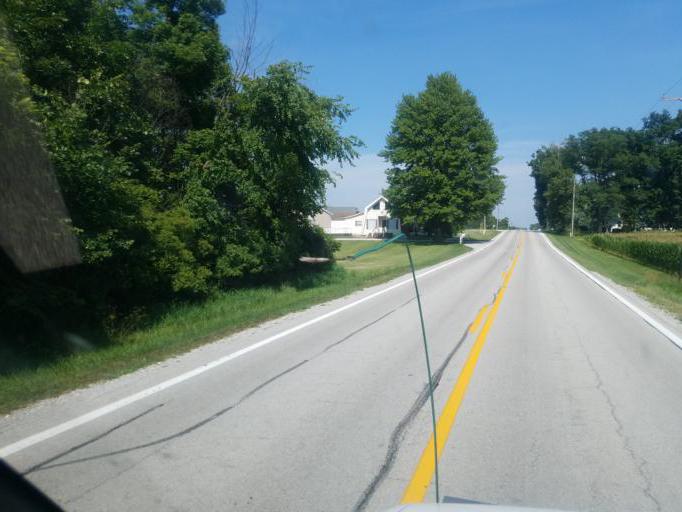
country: US
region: Ohio
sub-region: Shelby County
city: Botkins
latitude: 40.4968
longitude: -84.2202
